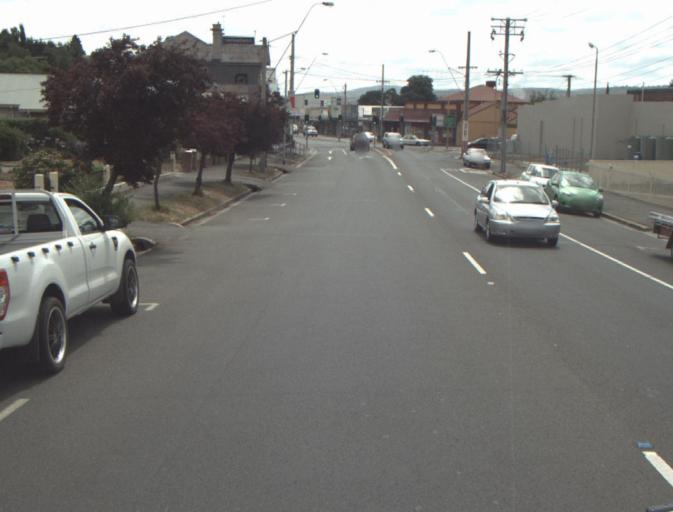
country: AU
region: Tasmania
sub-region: Launceston
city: Newstead
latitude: -41.4430
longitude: 147.1617
